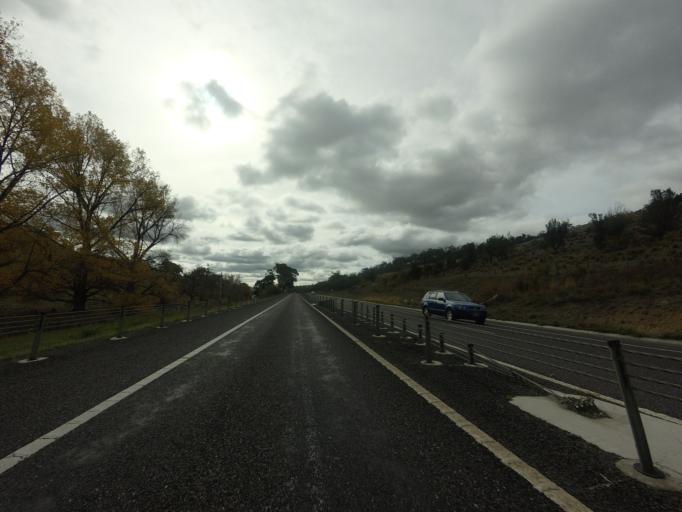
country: AU
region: Tasmania
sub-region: Brighton
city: Bridgewater
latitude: -42.5597
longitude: 147.2089
